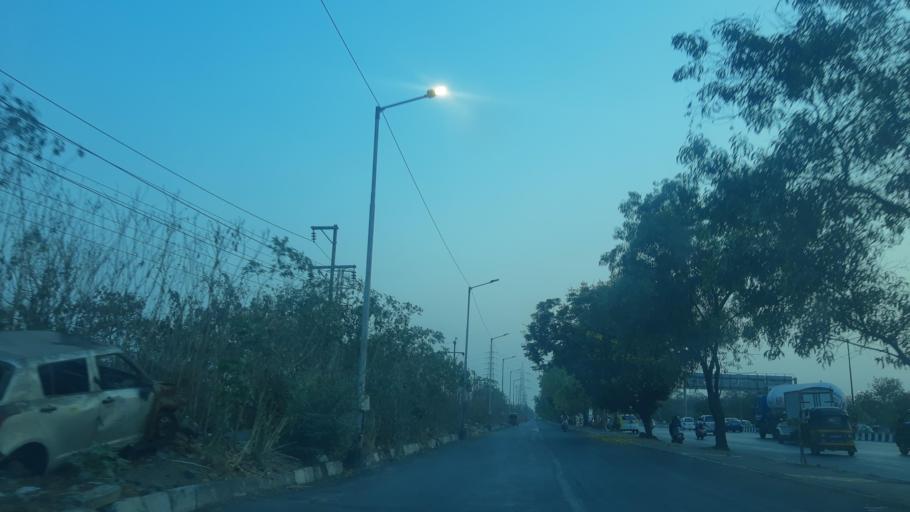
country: IN
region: Maharashtra
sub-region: Thane
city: Thane
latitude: 19.1622
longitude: 72.9623
